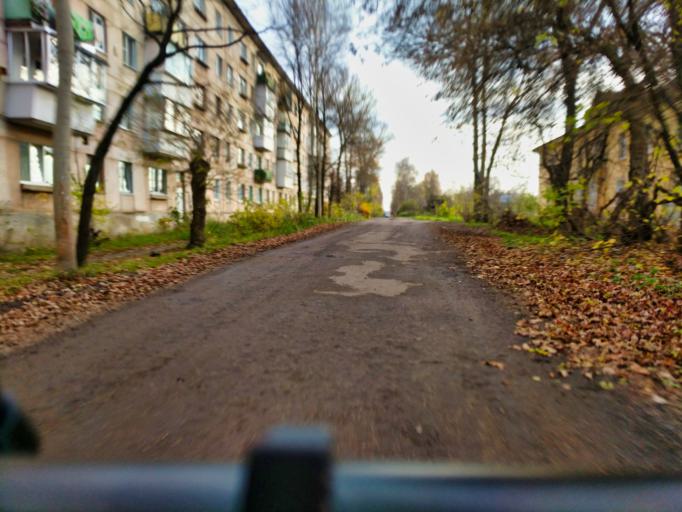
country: RU
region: Tverskaya
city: Rzhev
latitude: 56.2685
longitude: 34.3262
